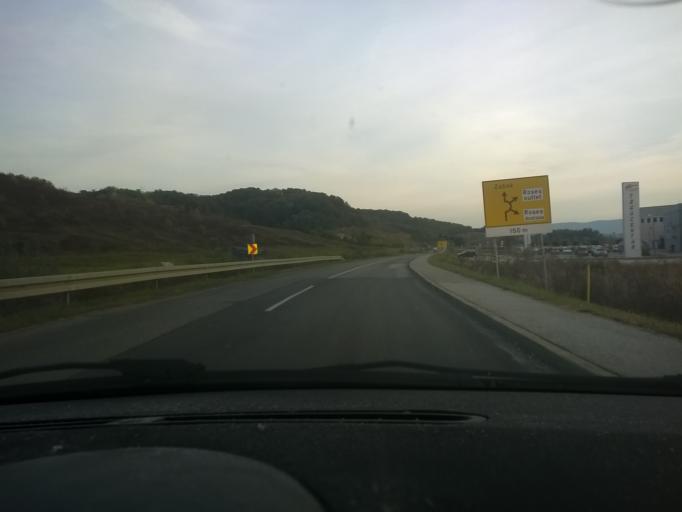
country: HR
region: Krapinsko-Zagorska
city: Zabok
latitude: 46.0894
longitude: 15.9124
